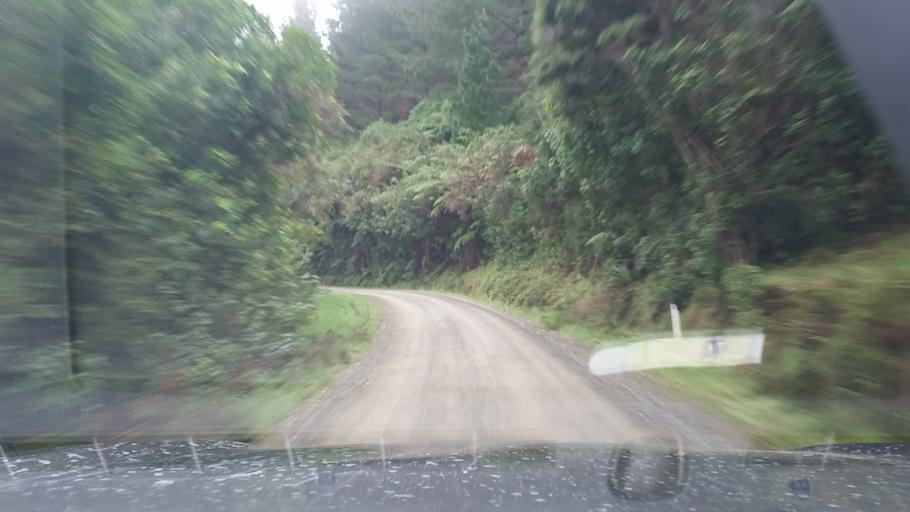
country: NZ
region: Marlborough
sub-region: Marlborough District
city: Picton
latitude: -41.1792
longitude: 173.9967
